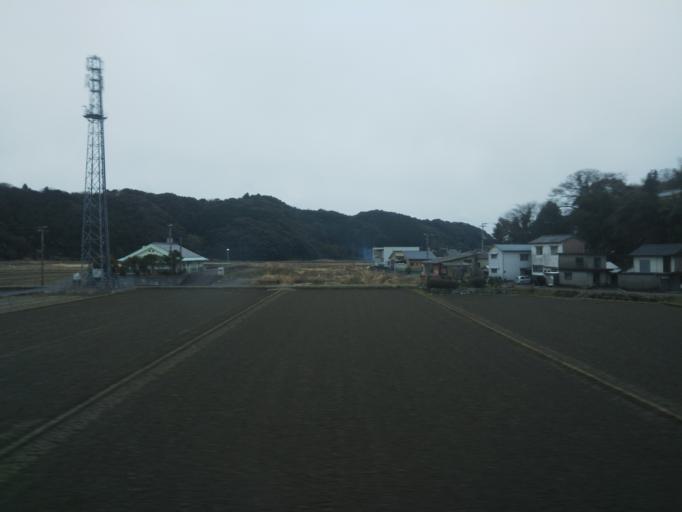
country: JP
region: Kochi
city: Nakamura
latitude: 32.9834
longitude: 132.9592
